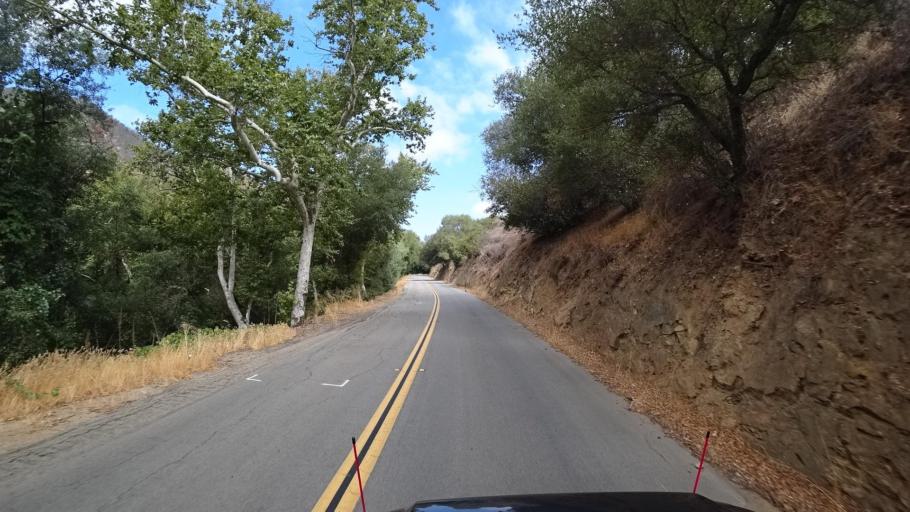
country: US
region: California
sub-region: San Diego County
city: Fallbrook
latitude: 33.4171
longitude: -117.2468
